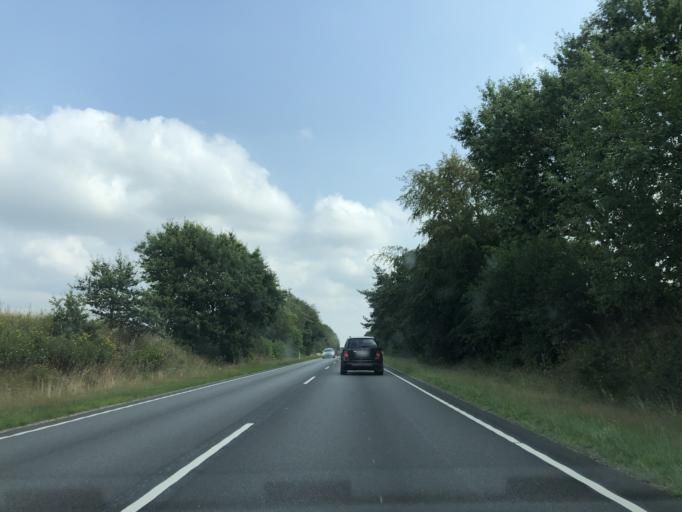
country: DK
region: Central Jutland
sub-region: Viborg Kommune
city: Bjerringbro
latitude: 56.3256
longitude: 9.5584
